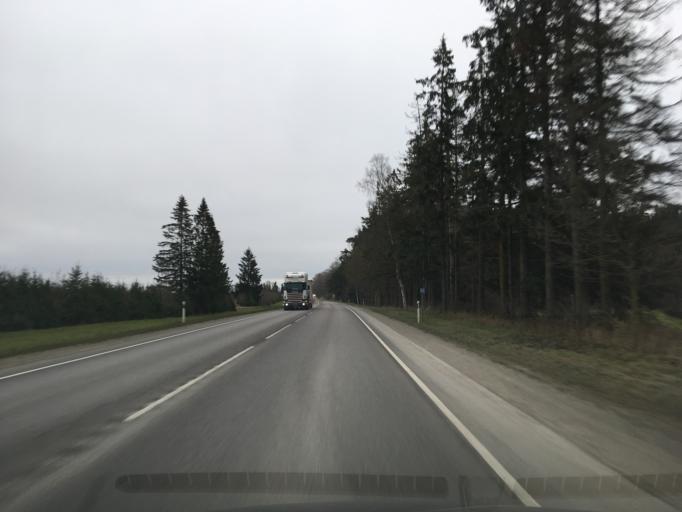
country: EE
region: Laeaene-Virumaa
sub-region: Rakvere linn
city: Rakvere
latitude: 59.3974
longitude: 26.3770
